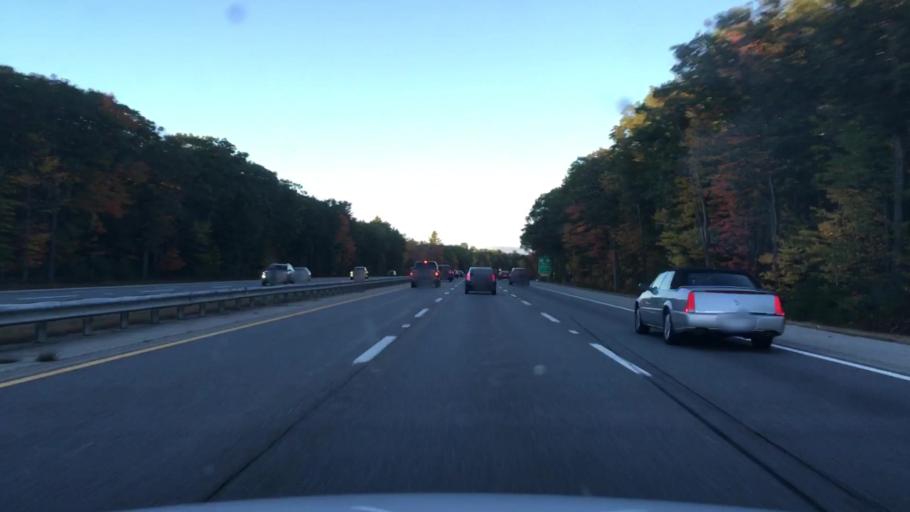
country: US
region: Maine
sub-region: York County
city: Wells Beach Station
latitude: 43.3079
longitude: -70.6148
